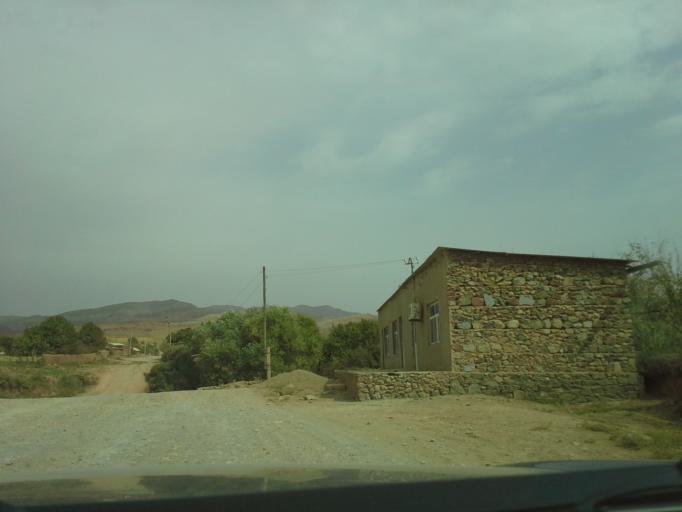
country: UZ
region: Qashqadaryo
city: Qorashina
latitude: 37.9264
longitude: 66.4939
